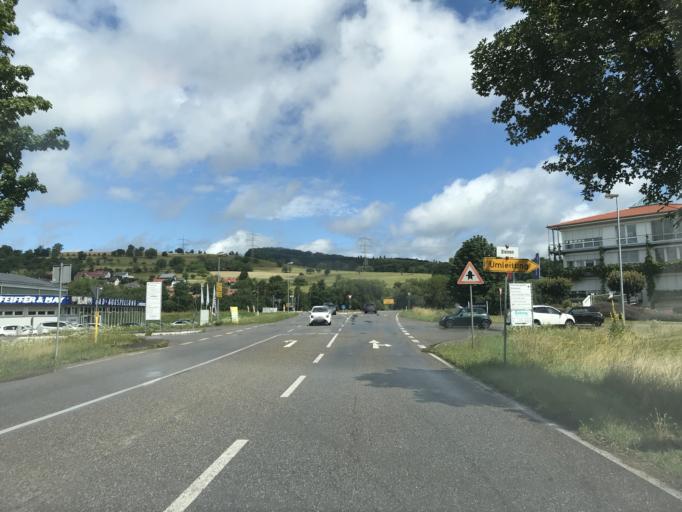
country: DE
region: Baden-Wuerttemberg
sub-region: Freiburg Region
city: Steinen
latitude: 47.6410
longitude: 7.7048
